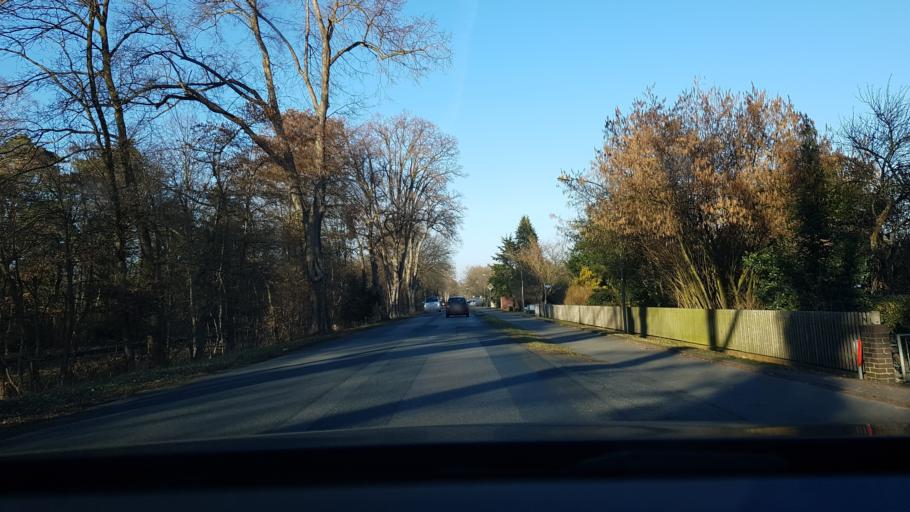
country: DE
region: Lower Saxony
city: Gifhorn
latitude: 52.5039
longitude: 10.5748
